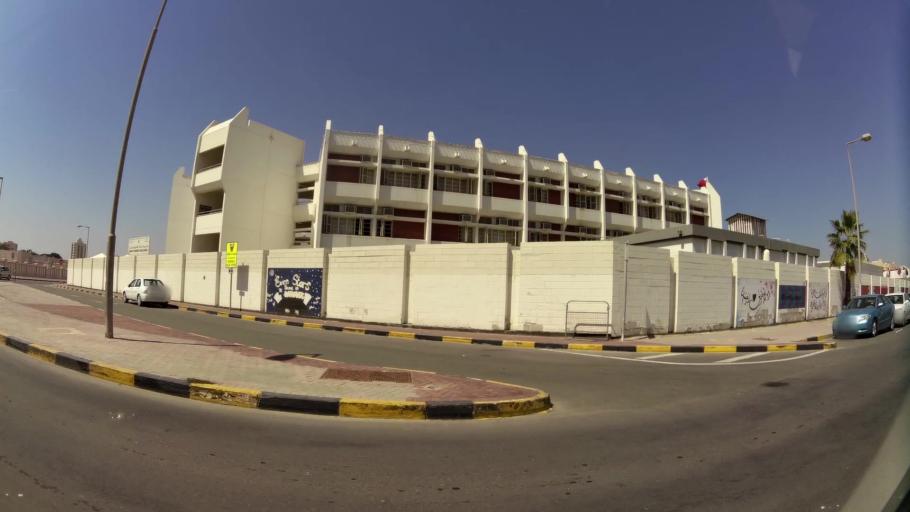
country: BH
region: Manama
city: Manama
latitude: 26.2208
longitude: 50.5946
